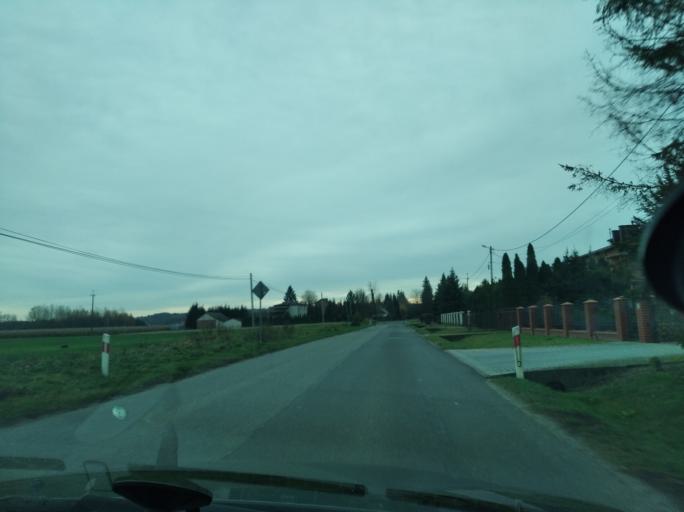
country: PL
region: Subcarpathian Voivodeship
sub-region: Powiat lancucki
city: Czarna
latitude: 50.0868
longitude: 22.1867
